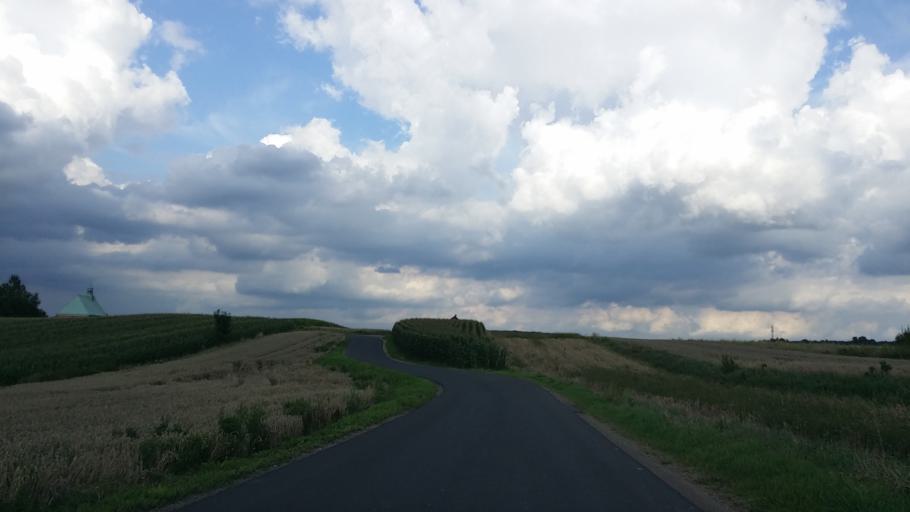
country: PL
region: Lesser Poland Voivodeship
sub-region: Powiat wadowicki
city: Bachowice
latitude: 49.9649
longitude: 19.4855
